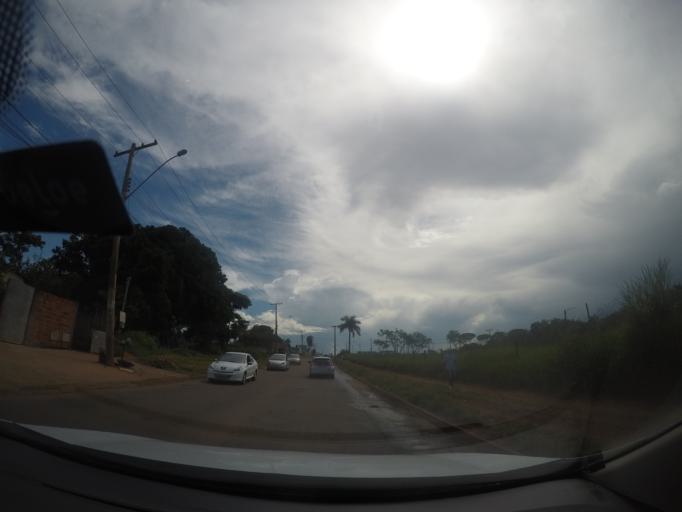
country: BR
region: Goias
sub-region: Goiania
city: Goiania
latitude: -16.6840
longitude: -49.3644
